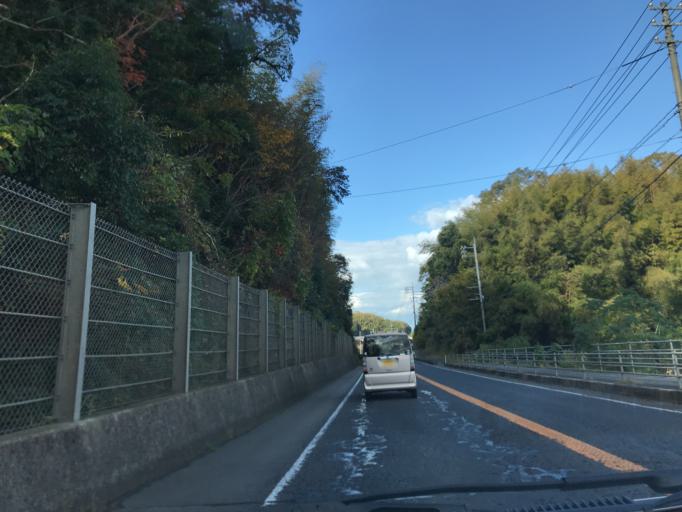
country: JP
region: Shimane
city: Yasugicho
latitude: 35.4252
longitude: 133.2822
